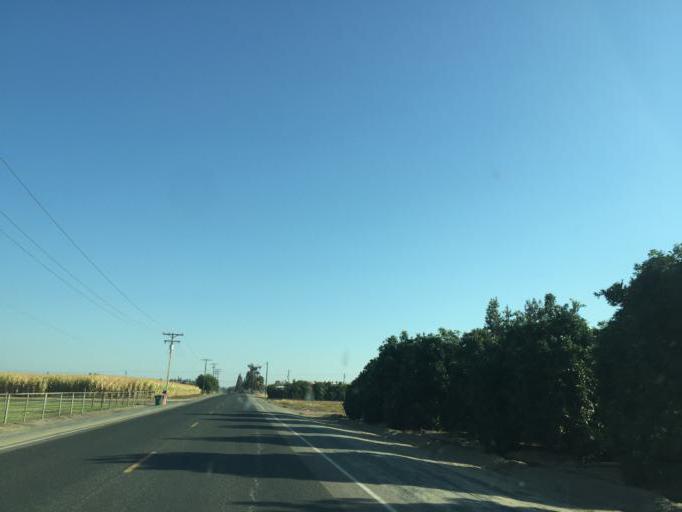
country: US
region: California
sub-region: Tulare County
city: Visalia
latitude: 36.3889
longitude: -119.2787
